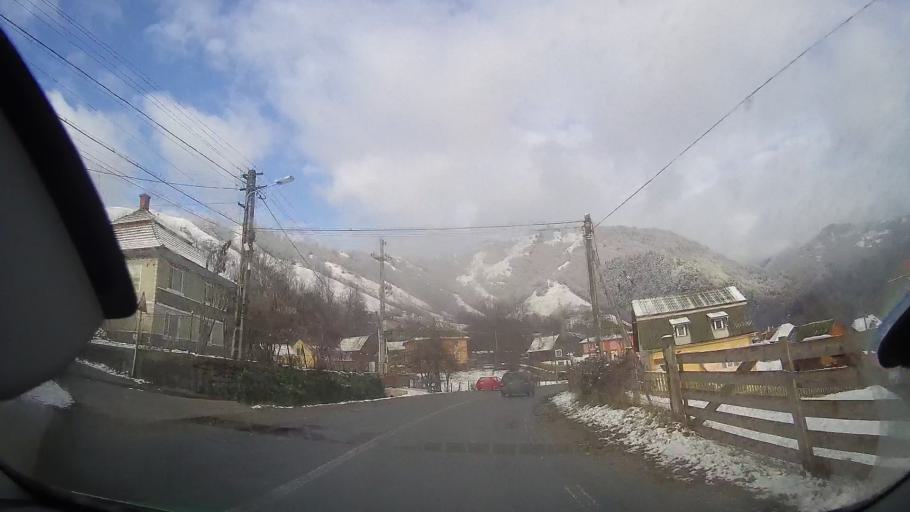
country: RO
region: Alba
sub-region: Oras Baia de Aries
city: Baia de Aries
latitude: 46.3941
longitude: 23.3000
